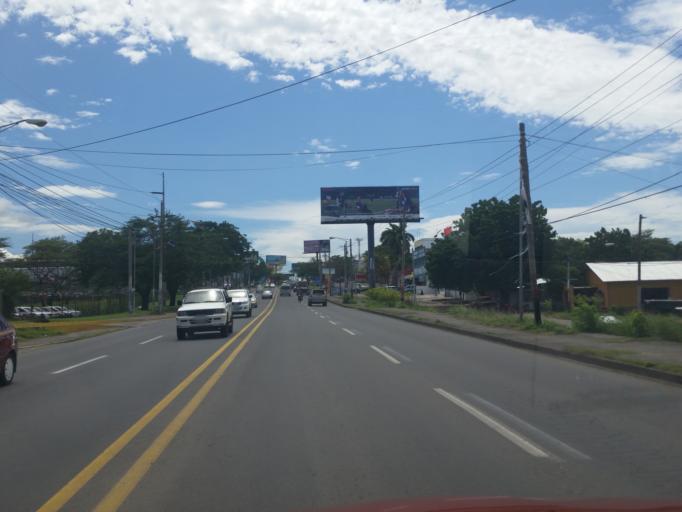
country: NI
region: Managua
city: Managua
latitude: 12.1249
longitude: -86.2795
